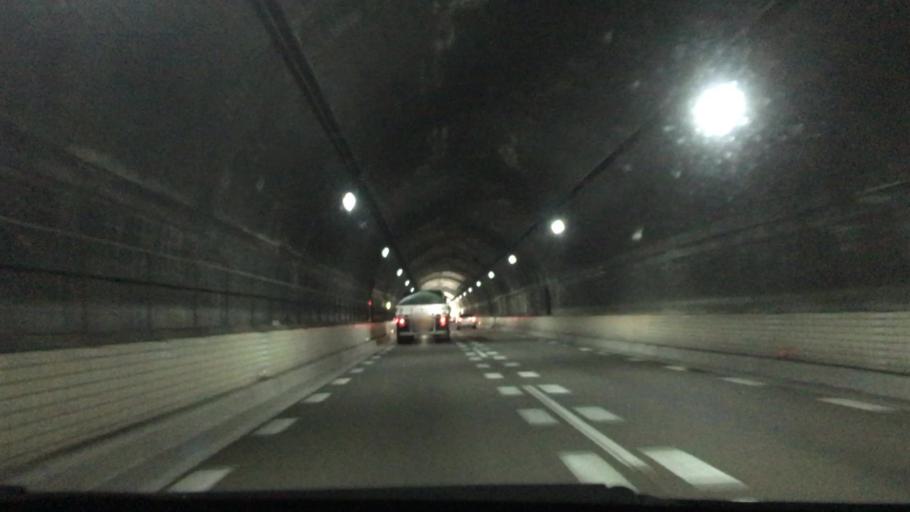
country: JP
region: Yamaguchi
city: Shimonoseki
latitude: 33.9565
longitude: 130.9693
